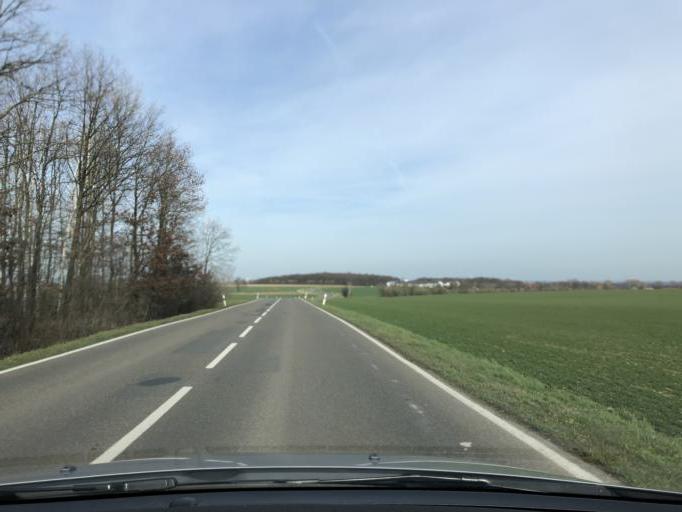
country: DE
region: Saxony-Anhalt
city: Osterfeld
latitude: 51.0655
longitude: 11.9746
